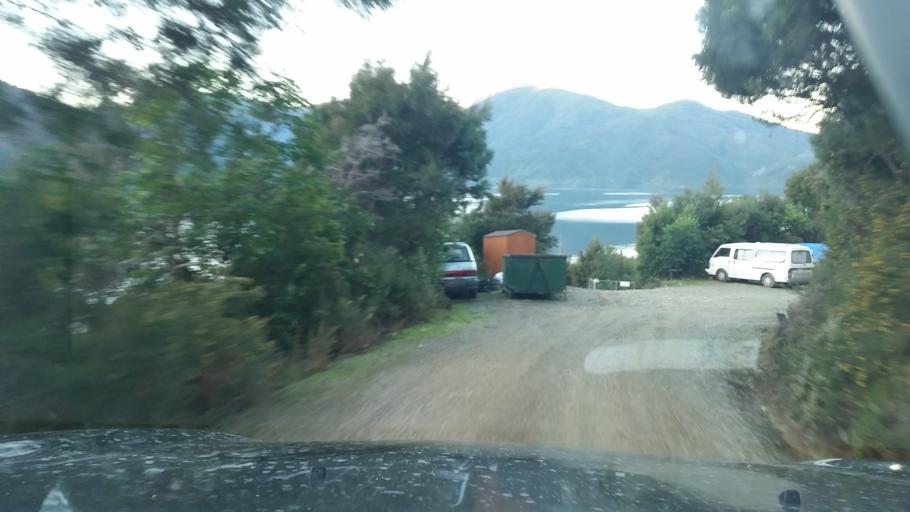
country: NZ
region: Marlborough
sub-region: Marlborough District
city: Picton
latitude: -41.1302
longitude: 174.1506
